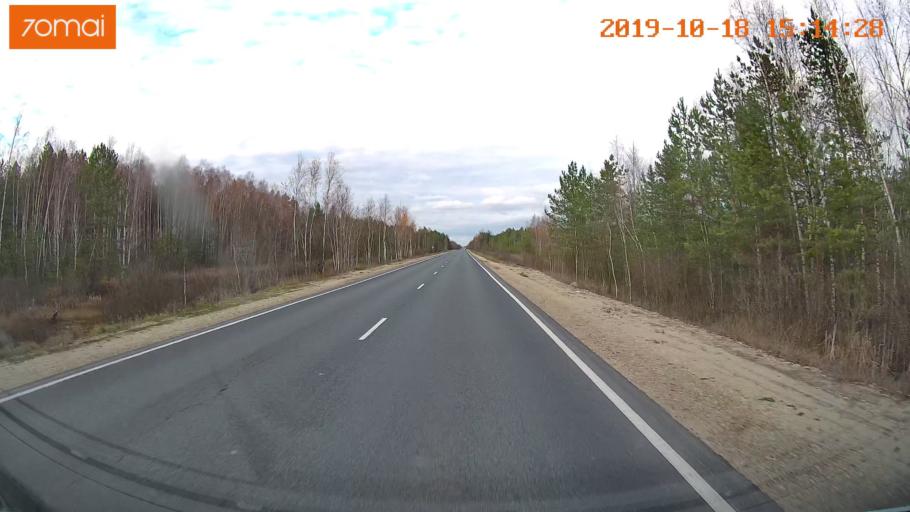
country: RU
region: Vladimir
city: Gus'-Khrustal'nyy
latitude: 55.6031
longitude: 40.7203
